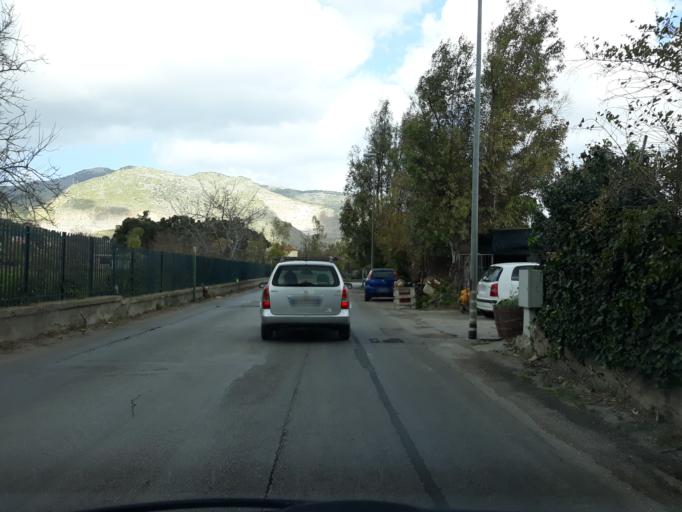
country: IT
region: Sicily
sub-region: Palermo
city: Piano dei Geli
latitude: 38.1149
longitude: 13.3037
